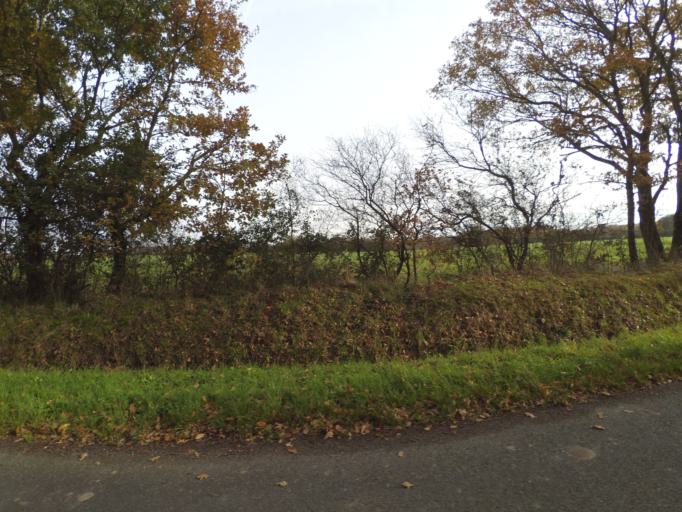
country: FR
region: Pays de la Loire
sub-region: Departement de la Loire-Atlantique
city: La Planche
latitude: 47.0081
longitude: -1.3915
